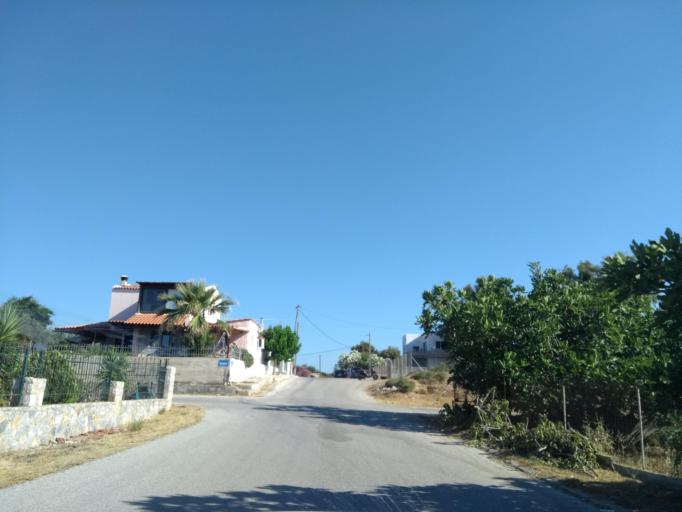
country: GR
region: Crete
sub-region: Nomos Chanias
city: Pithari
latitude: 35.5889
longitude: 24.0917
